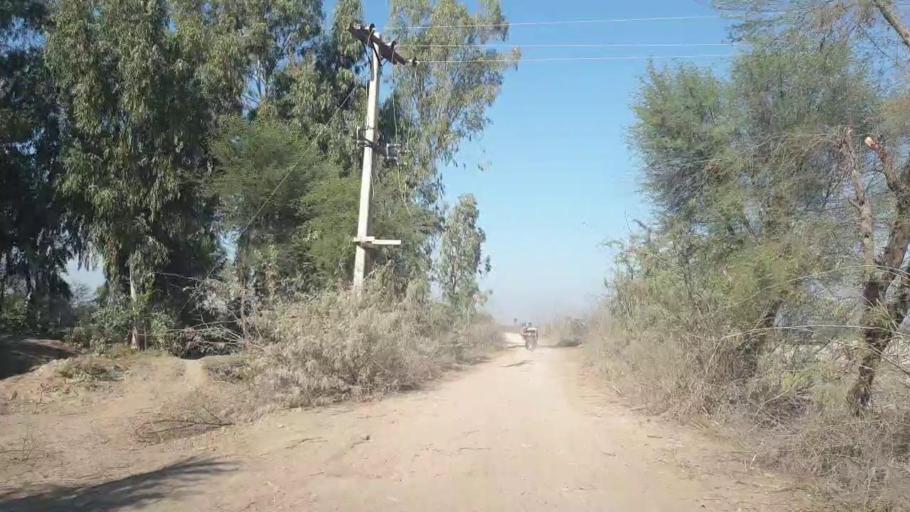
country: PK
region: Sindh
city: Mirpur Mathelo
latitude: 28.0958
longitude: 69.5321
